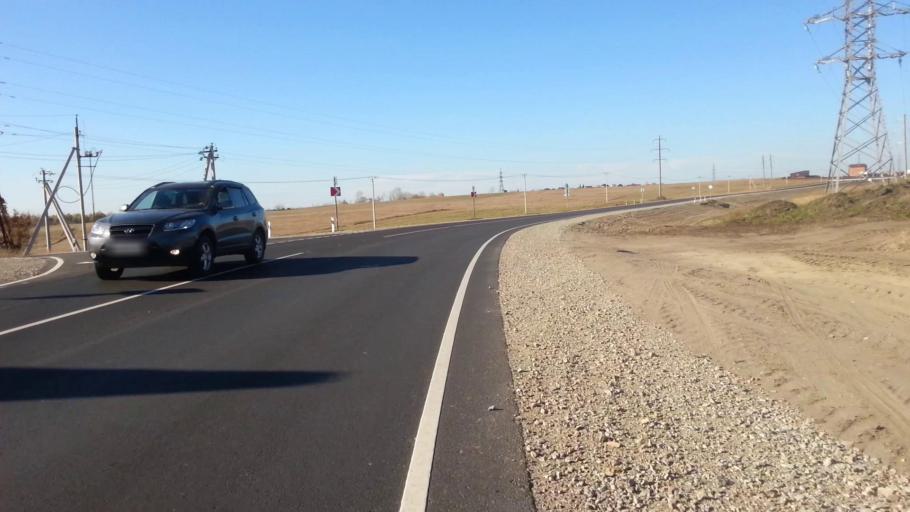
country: RU
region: Altai Krai
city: Sannikovo
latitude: 53.3291
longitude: 83.9393
